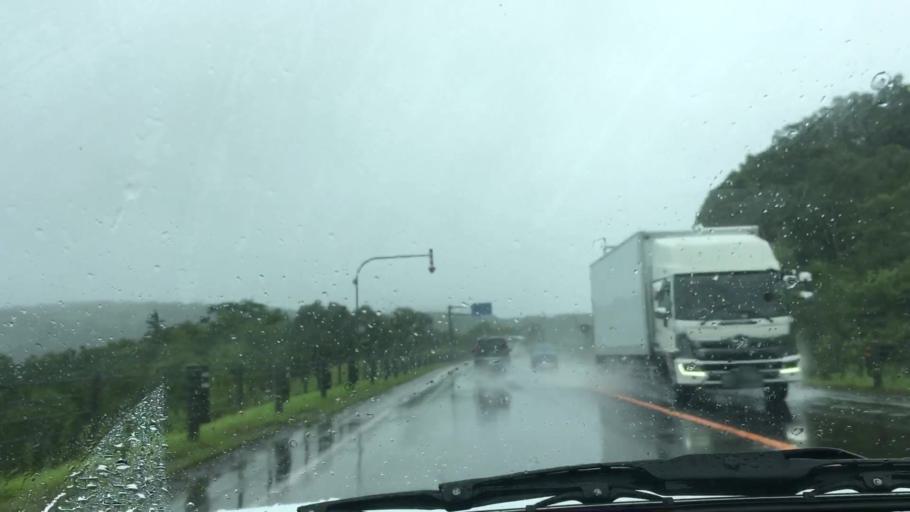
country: JP
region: Hokkaido
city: Sapporo
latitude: 42.8613
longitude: 141.1033
